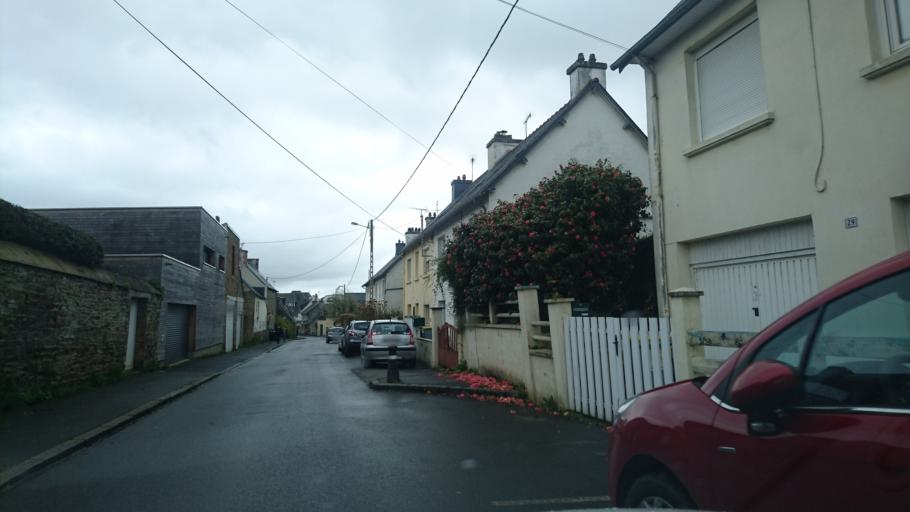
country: FR
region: Brittany
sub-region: Departement des Cotes-d'Armor
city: Lannion
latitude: 48.7303
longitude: -3.4495
